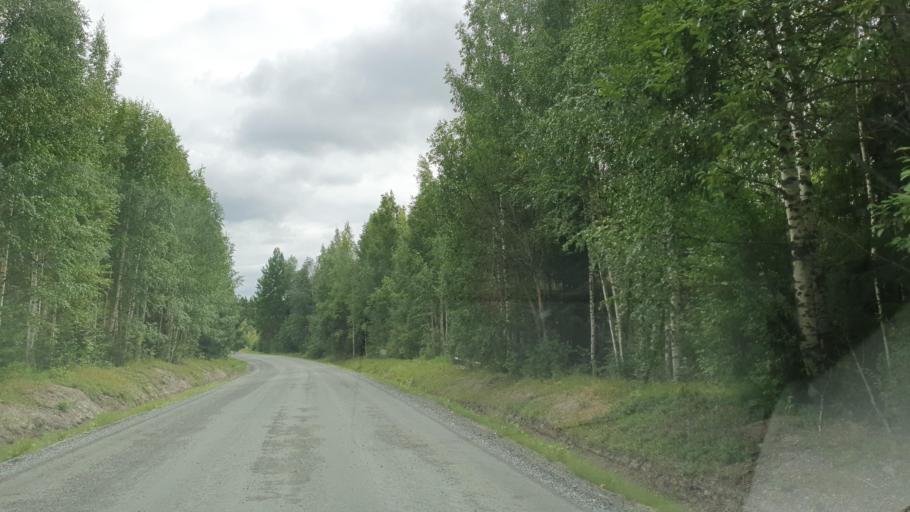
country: FI
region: Northern Savo
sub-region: Ylae-Savo
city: Iisalmi
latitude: 63.5303
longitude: 27.0885
